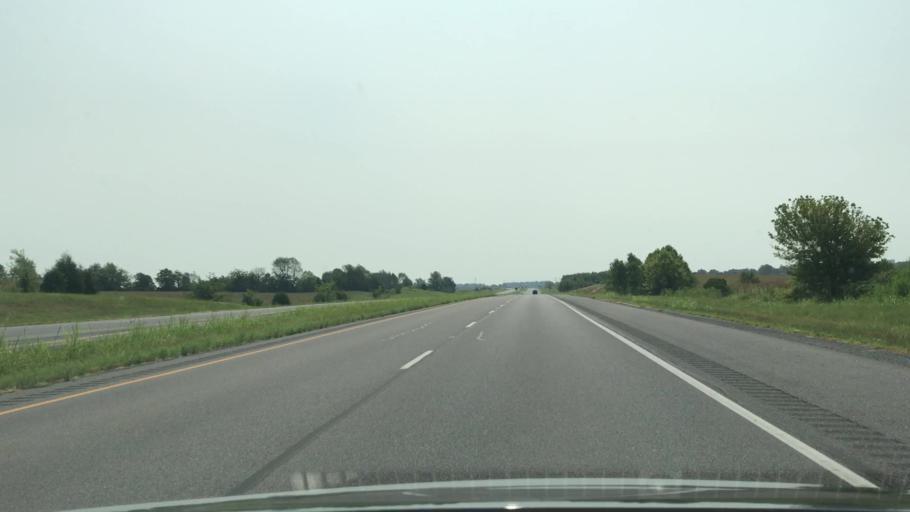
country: US
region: Kentucky
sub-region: Graves County
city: Mayfield
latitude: 36.6895
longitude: -88.5497
